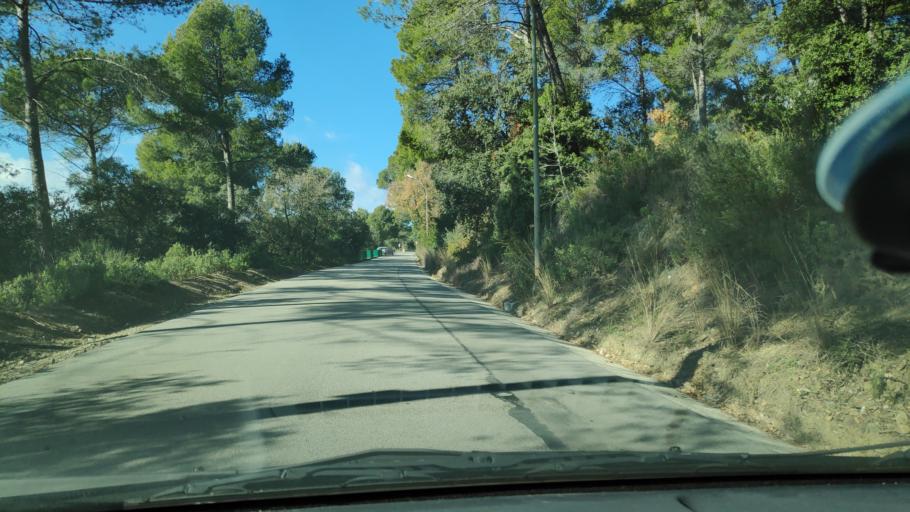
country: ES
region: Catalonia
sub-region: Provincia de Barcelona
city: Matadepera
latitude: 41.5972
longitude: 2.0121
